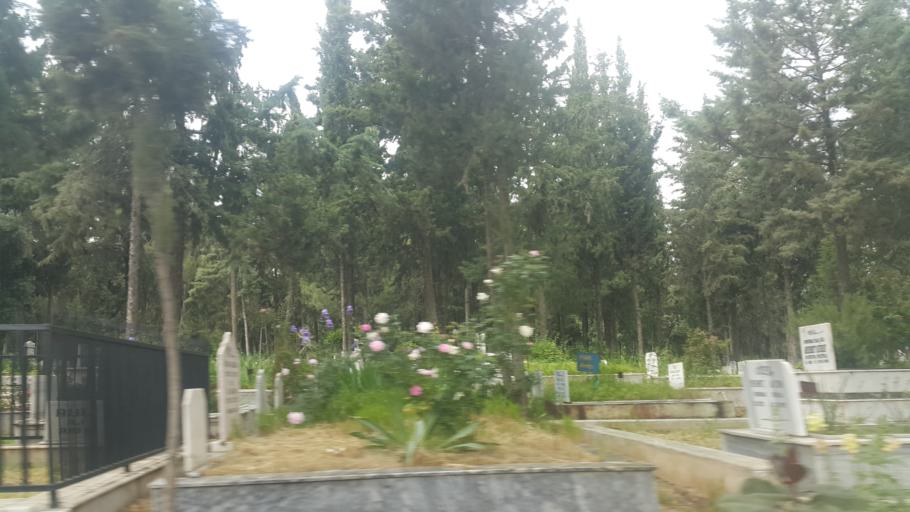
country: TR
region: Mersin
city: Mercin
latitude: 36.8180
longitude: 34.6060
